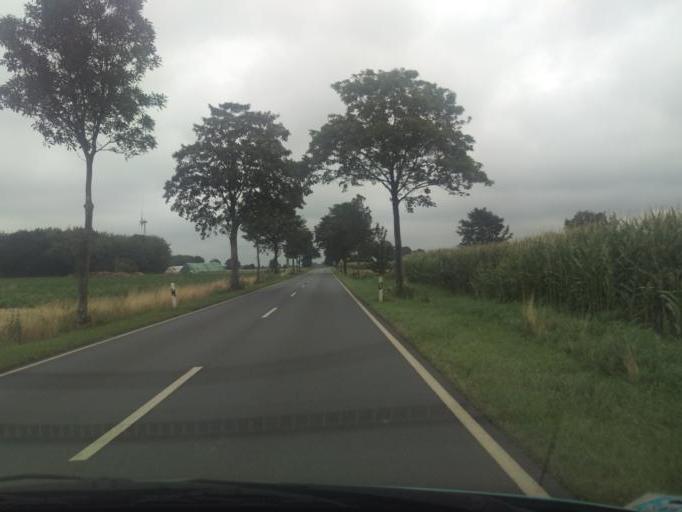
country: DE
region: Lower Saxony
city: Arpke
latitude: 52.3776
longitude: 10.1392
